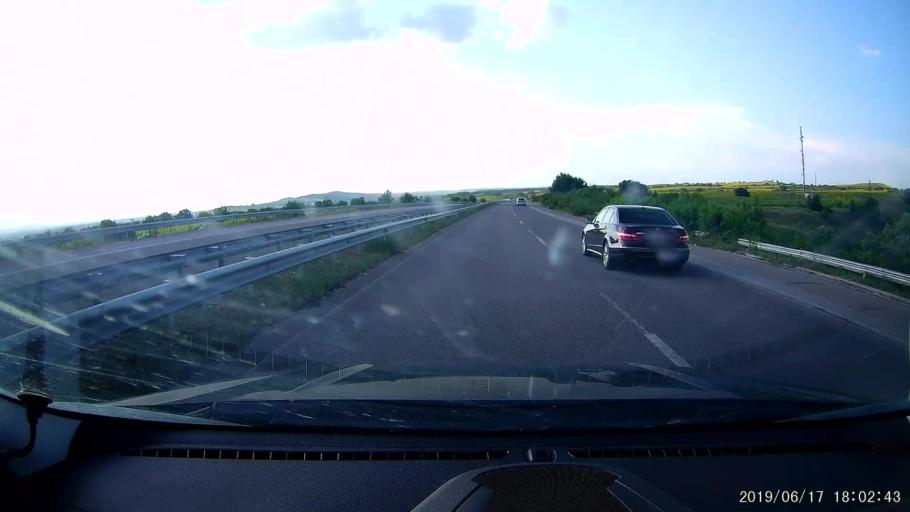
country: BG
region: Khaskovo
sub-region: Obshtina Svilengrad
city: Svilengrad
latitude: 41.7646
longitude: 26.2273
